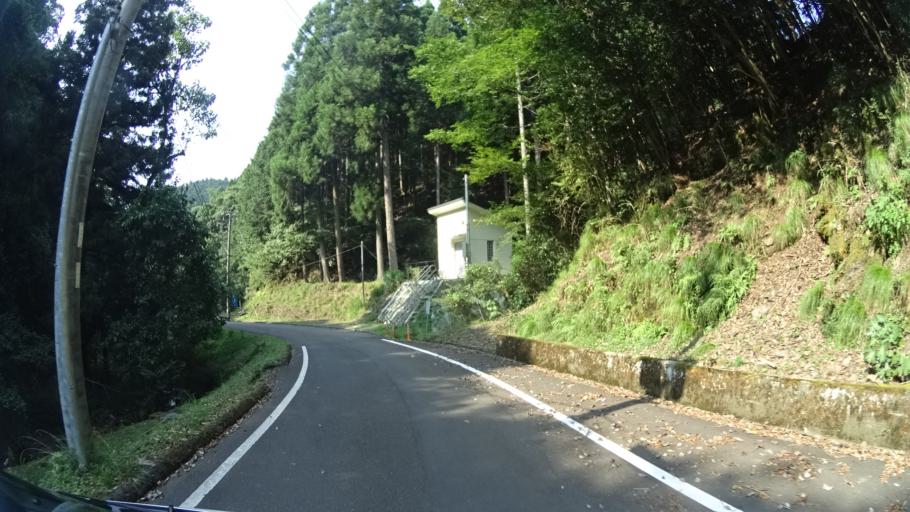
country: JP
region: Kyoto
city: Maizuru
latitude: 35.4045
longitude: 135.2408
